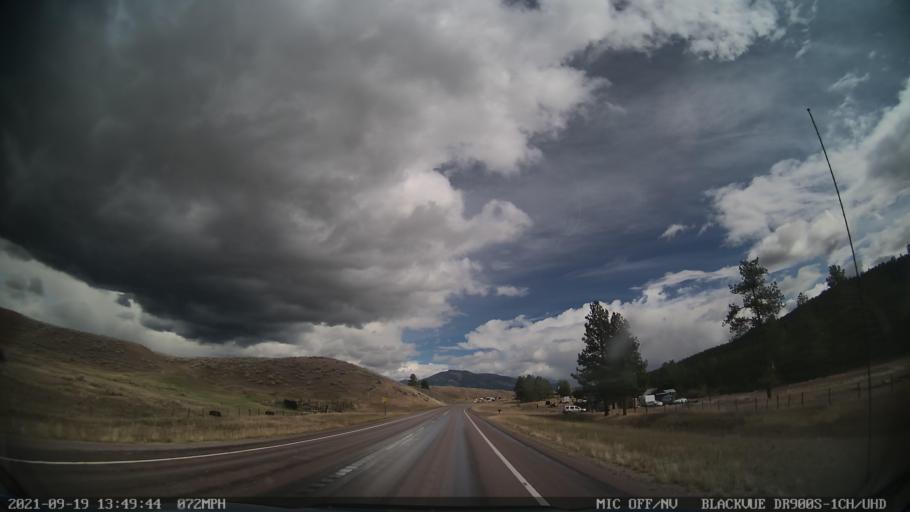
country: US
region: Montana
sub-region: Missoula County
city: Seeley Lake
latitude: 47.0421
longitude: -113.2165
